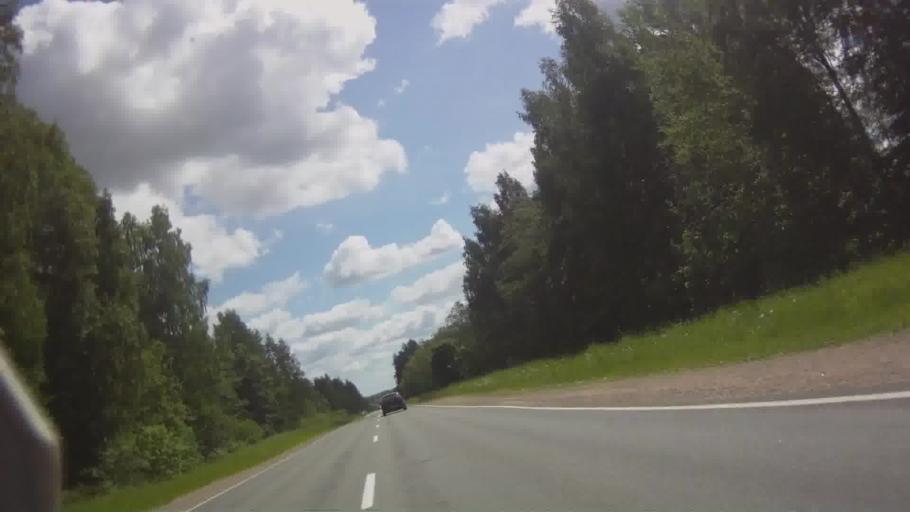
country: LV
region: Varaklani
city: Varaklani
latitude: 56.6073
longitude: 26.8469
